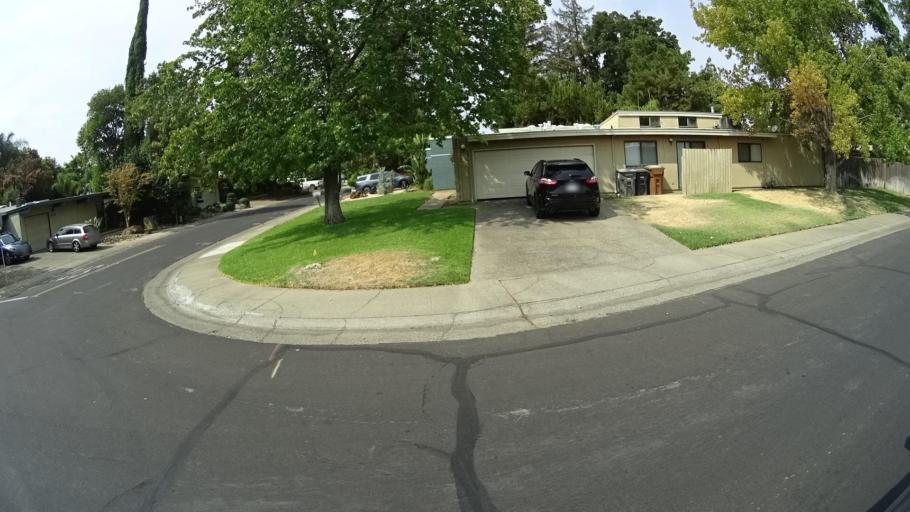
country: US
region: California
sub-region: Sacramento County
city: Elk Grove
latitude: 38.4137
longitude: -121.3792
